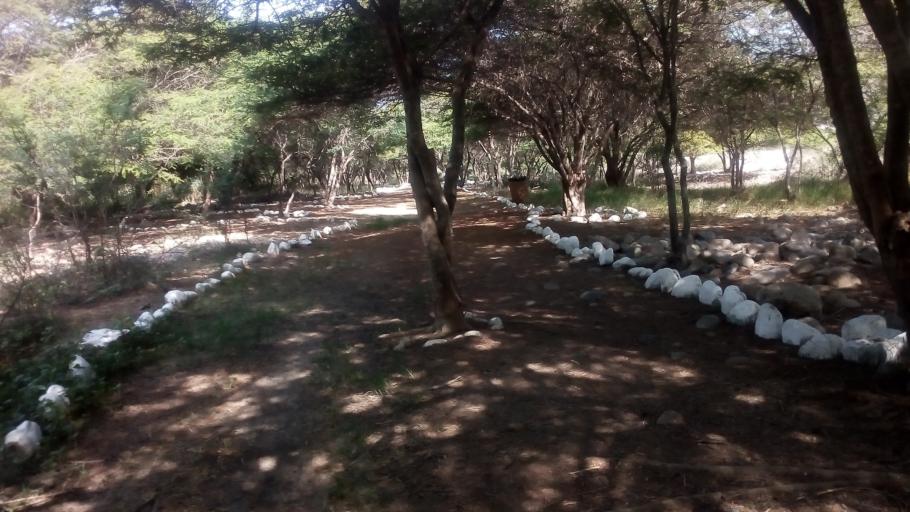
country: PE
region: Lima
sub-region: Huaura
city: Vegueta
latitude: -10.8933
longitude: -77.5130
